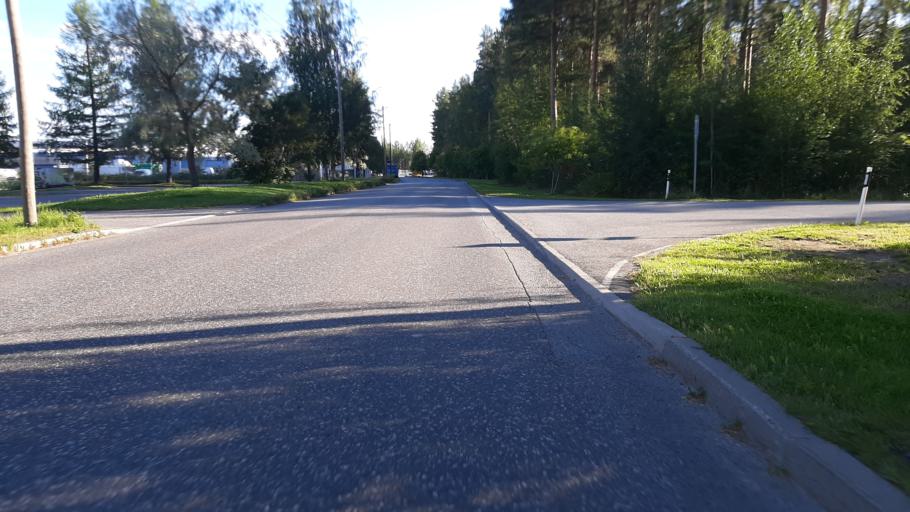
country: FI
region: North Karelia
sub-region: Joensuu
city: Joensuu
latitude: 62.6255
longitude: 29.7710
